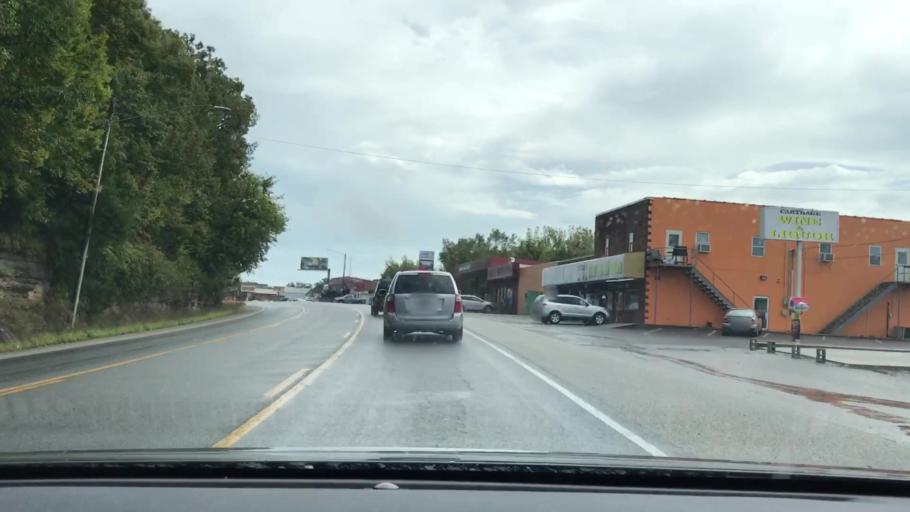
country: US
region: Tennessee
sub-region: Smith County
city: Carthage
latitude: 36.2633
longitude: -85.9555
